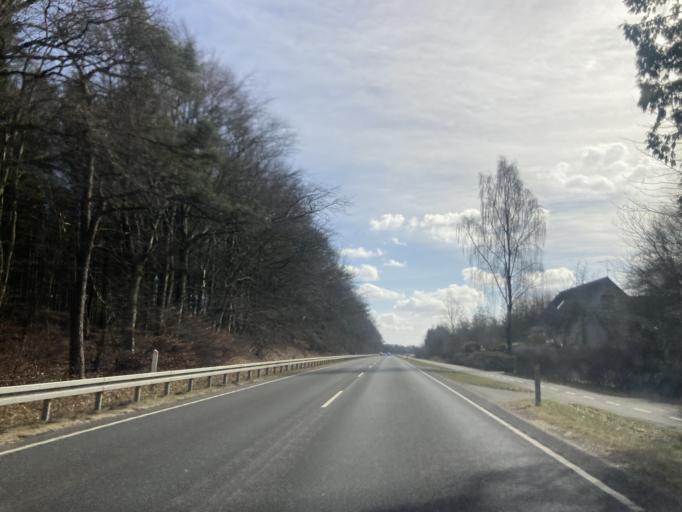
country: DK
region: Central Jutland
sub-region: Hedensted Kommune
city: Torring
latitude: 56.0011
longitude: 9.3846
